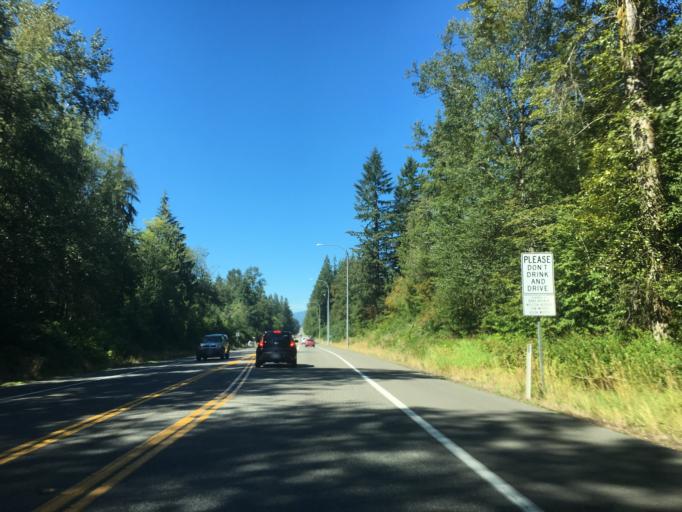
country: US
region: Washington
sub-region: Snohomish County
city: Sisco Heights
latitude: 48.0901
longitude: -122.1118
